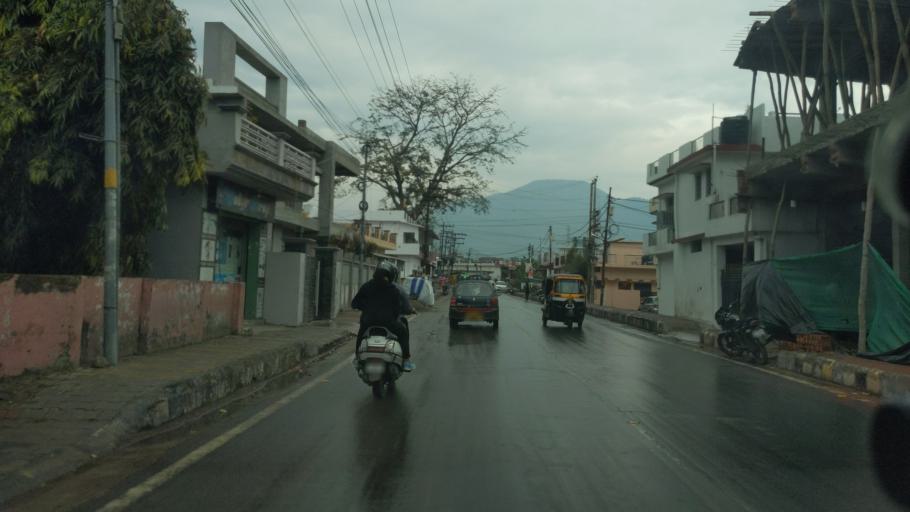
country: IN
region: Uttarakhand
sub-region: Naini Tal
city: Haldwani
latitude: 29.2430
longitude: 79.5302
